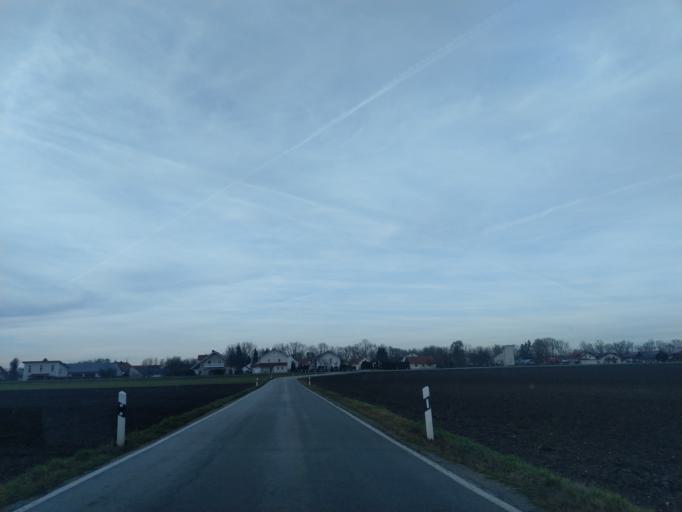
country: DE
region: Bavaria
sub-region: Lower Bavaria
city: Oberporing
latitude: 48.7131
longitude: 12.8501
